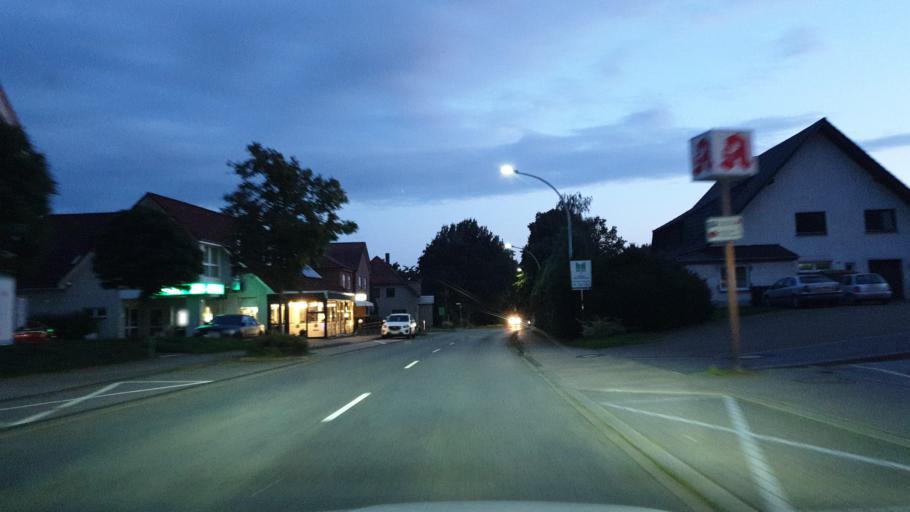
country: DE
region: North Rhine-Westphalia
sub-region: Regierungsbezirk Detmold
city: Huellhorst
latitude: 52.2730
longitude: 8.7103
